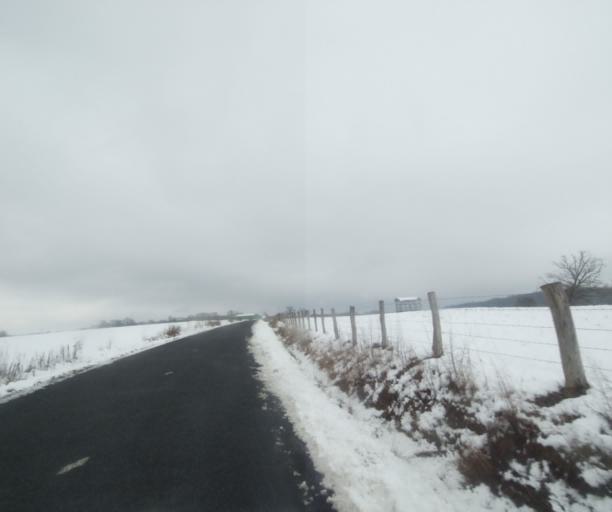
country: FR
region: Champagne-Ardenne
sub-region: Departement de la Haute-Marne
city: Montier-en-Der
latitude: 48.4701
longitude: 4.8029
